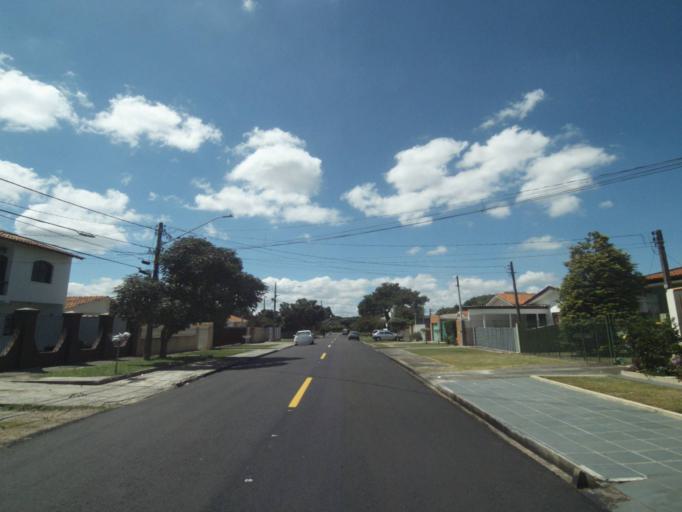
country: BR
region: Parana
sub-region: Pinhais
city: Pinhais
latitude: -25.4425
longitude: -49.2130
